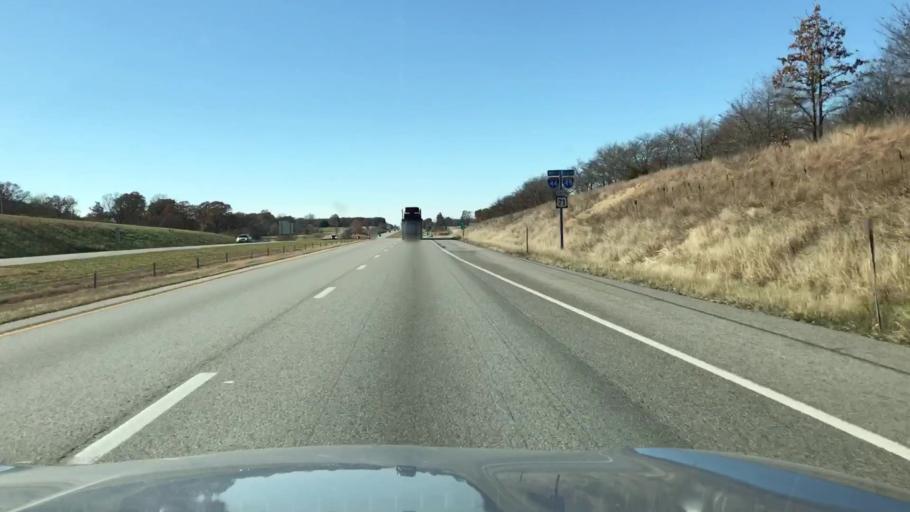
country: US
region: Missouri
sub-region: Jasper County
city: Duenweg
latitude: 37.0821
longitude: -94.3202
